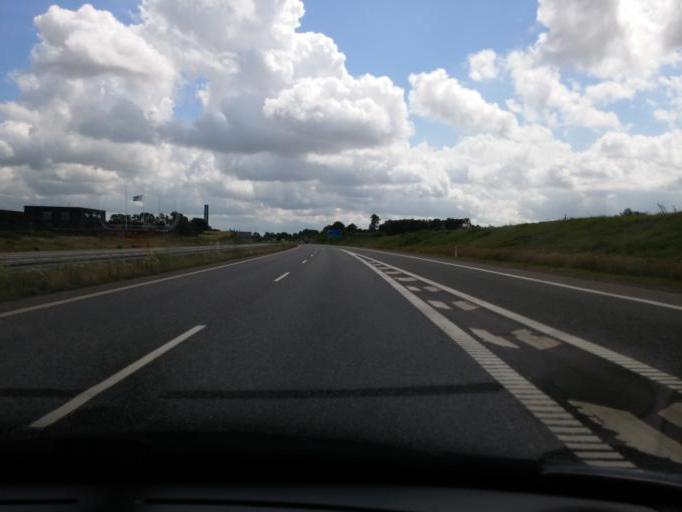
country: DK
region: South Denmark
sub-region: Faaborg-Midtfyn Kommune
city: Ringe
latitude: 55.2533
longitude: 10.4731
